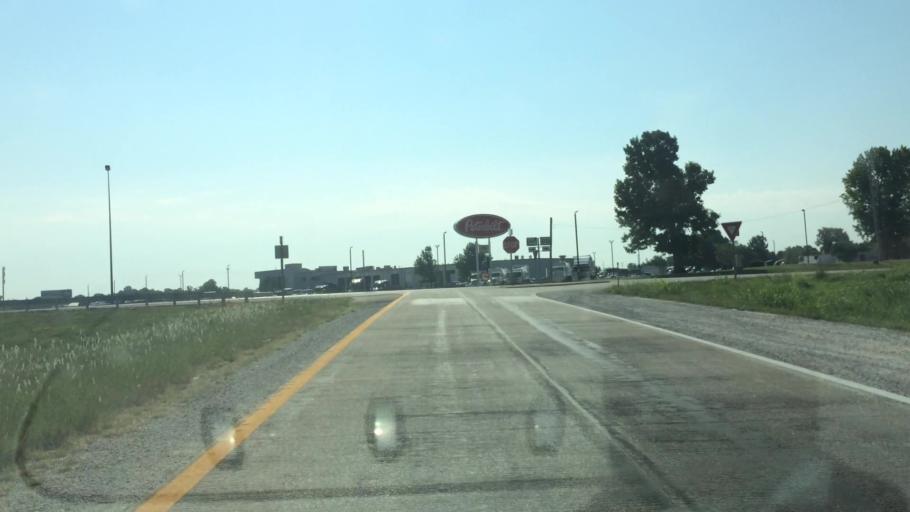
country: US
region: Missouri
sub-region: Greene County
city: Strafford
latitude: 37.2498
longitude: -93.1841
